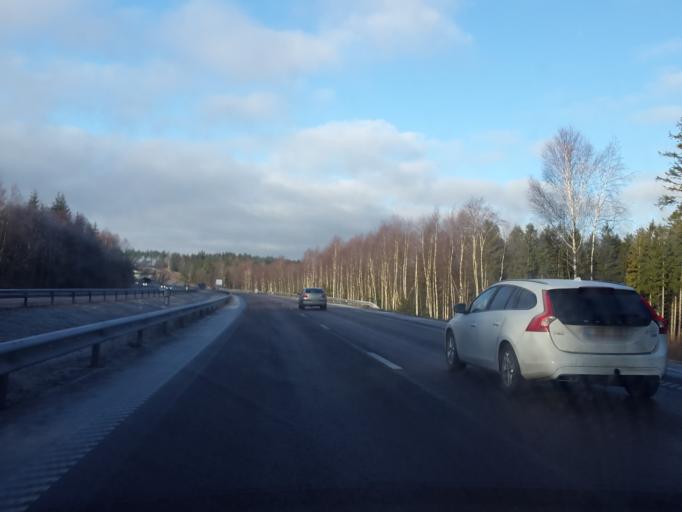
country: SE
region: Vaestra Goetaland
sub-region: Harryda Kommun
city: Landvetter
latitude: 57.7422
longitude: 12.2007
